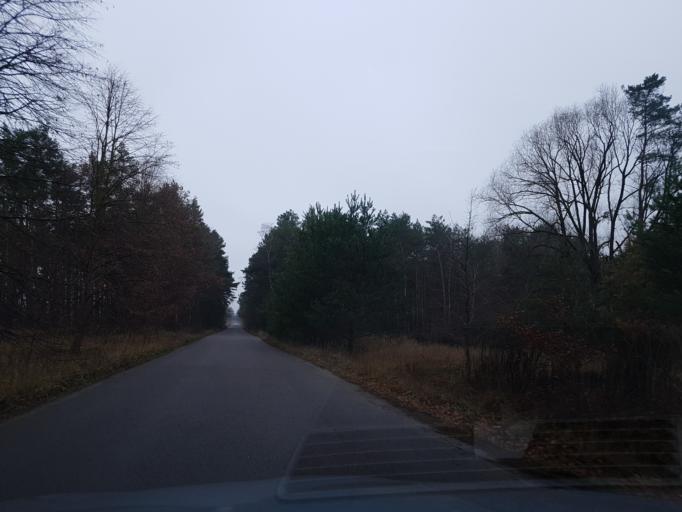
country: DE
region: Brandenburg
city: Schilda
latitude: 51.5991
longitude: 13.3868
